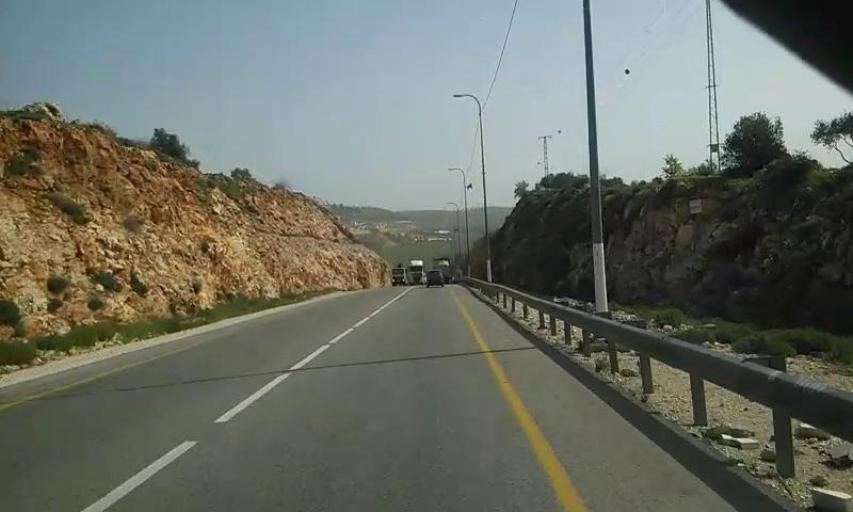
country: PS
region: West Bank
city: Turmus`ayya
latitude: 32.0471
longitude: 35.2896
